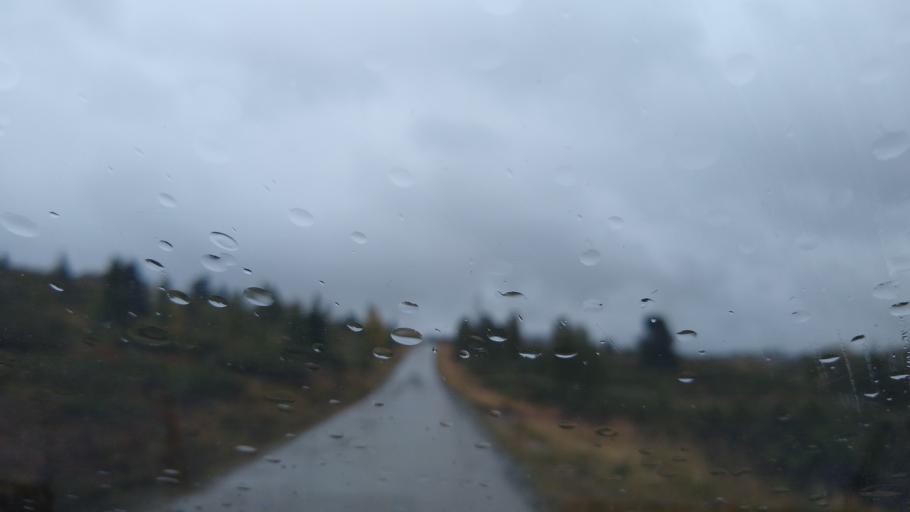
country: NO
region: Oppland
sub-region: Ringebu
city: Ringebu
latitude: 61.6729
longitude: 10.0917
